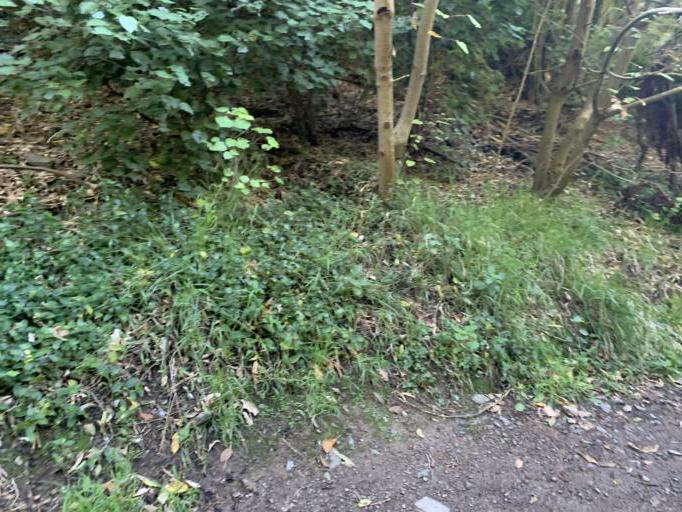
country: NZ
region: Wellington
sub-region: Wellington City
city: Kelburn
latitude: -41.2964
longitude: 174.7557
